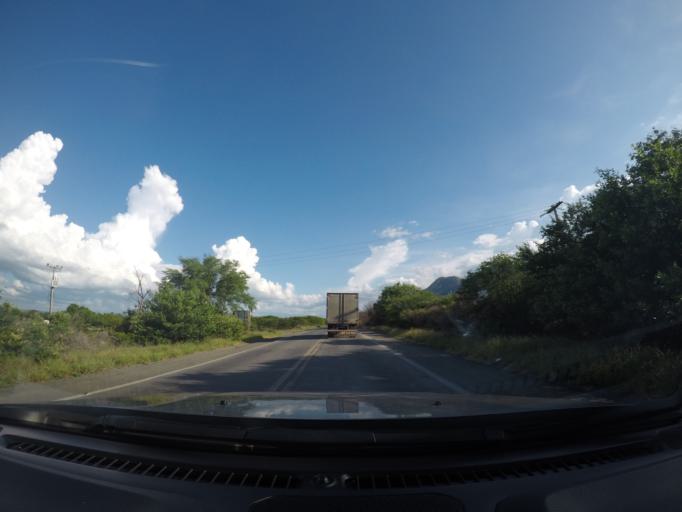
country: BR
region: Bahia
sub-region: Oliveira Dos Brejinhos
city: Oliveira dos Brejinhos
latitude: -12.0462
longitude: -42.9712
